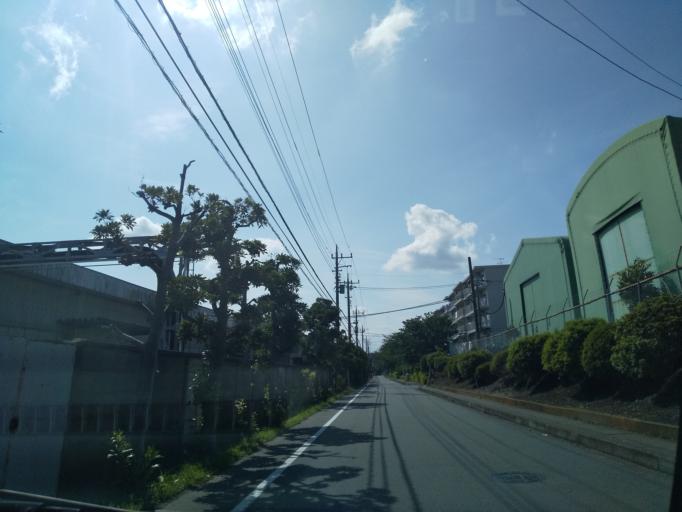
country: JP
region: Kanagawa
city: Zama
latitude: 35.4608
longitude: 139.4138
